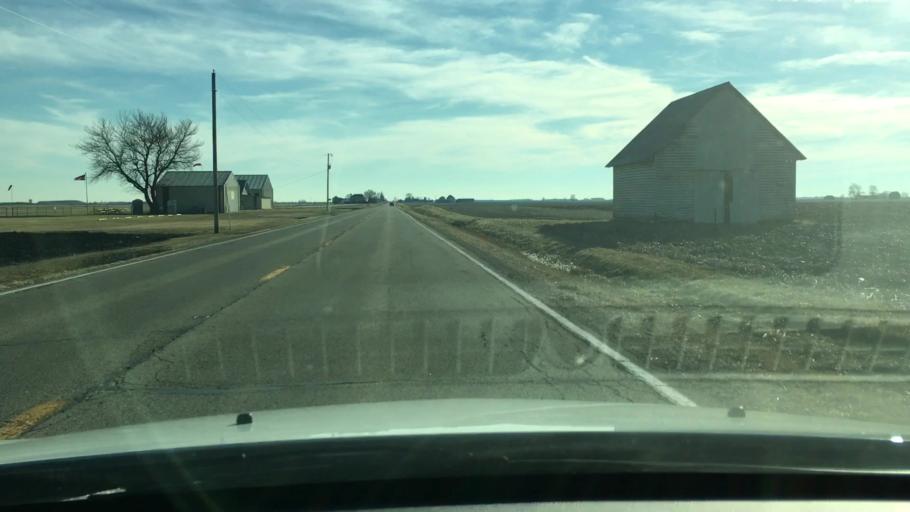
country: US
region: Illinois
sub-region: LaSalle County
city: Peru
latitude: 41.4216
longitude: -89.1264
